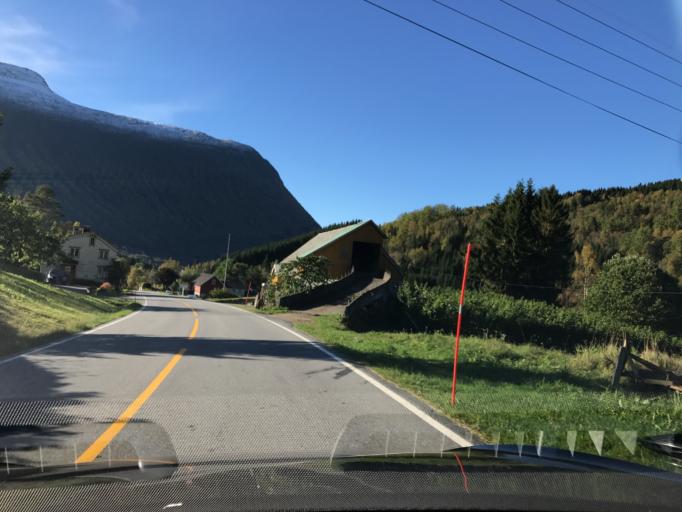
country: NO
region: More og Romsdal
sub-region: Norddal
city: Valldal
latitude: 62.3398
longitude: 7.3939
